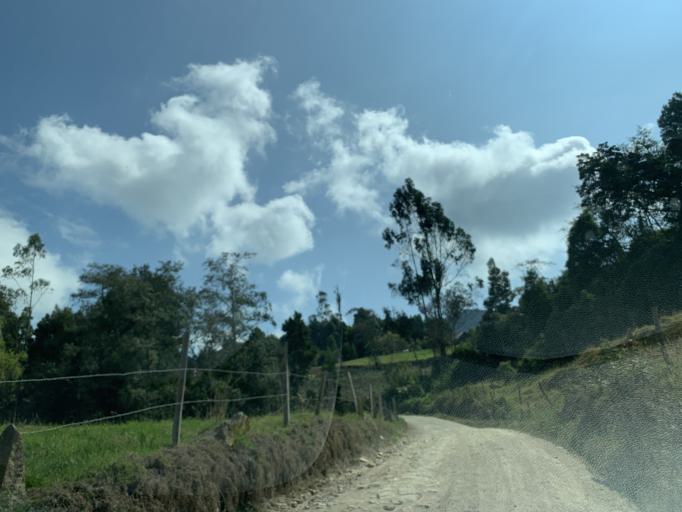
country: CO
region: Boyaca
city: Turmeque
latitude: 5.2793
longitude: -73.5031
